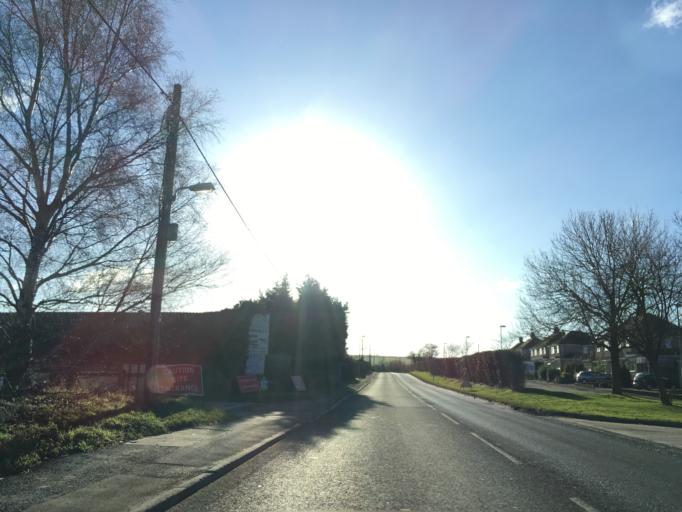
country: GB
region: England
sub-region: Borough of Swindon
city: Wroughton
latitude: 51.5308
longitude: -1.7853
